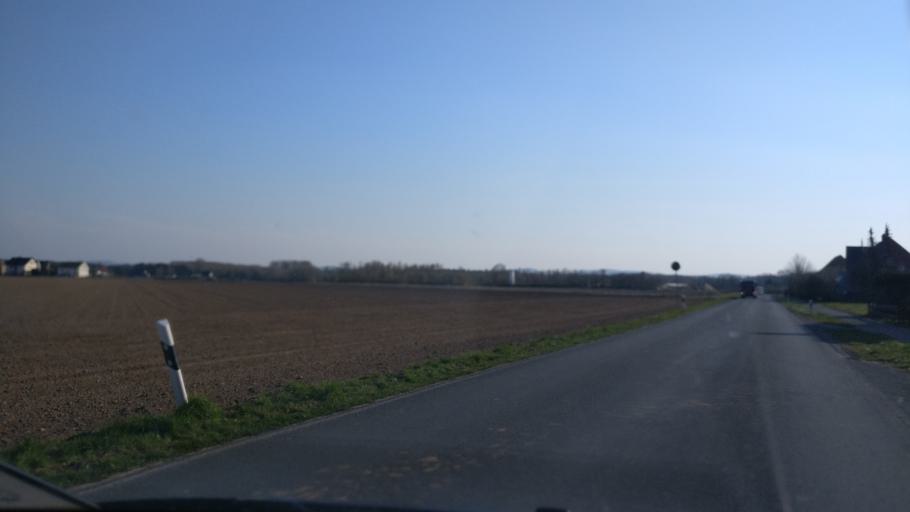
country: DE
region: North Rhine-Westphalia
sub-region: Regierungsbezirk Detmold
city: Lage
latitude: 52.0242
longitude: 8.7577
